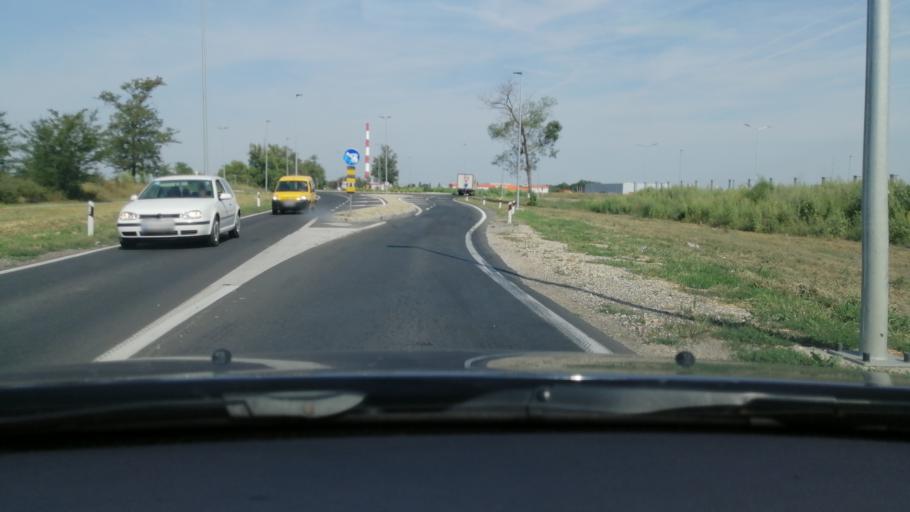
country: RS
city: Ecka
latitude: 45.3438
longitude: 20.4285
